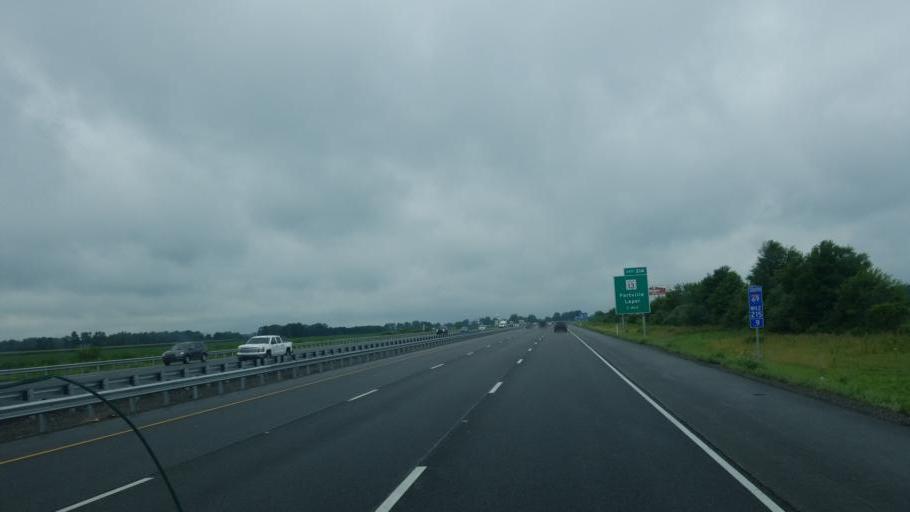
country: US
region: Indiana
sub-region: Madison County
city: Ingalls
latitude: 39.9916
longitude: -85.8161
